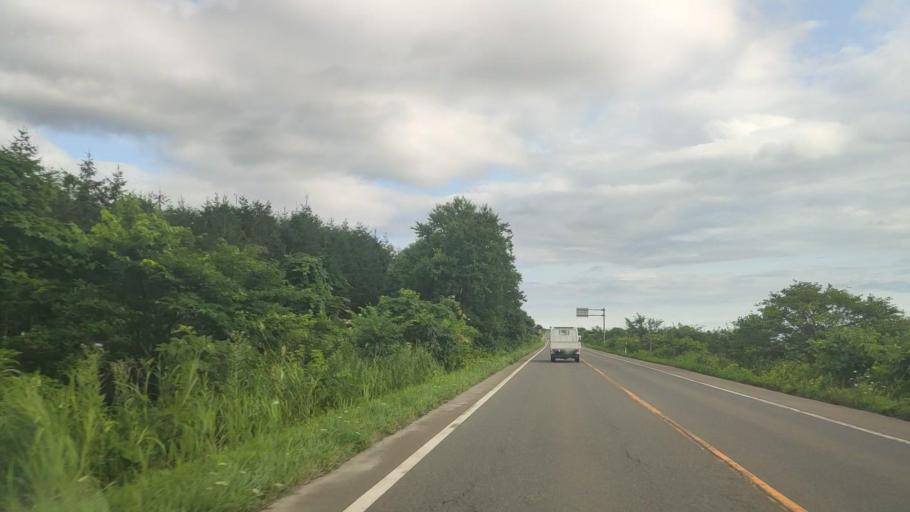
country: JP
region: Hokkaido
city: Niseko Town
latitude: 42.5840
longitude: 140.4517
